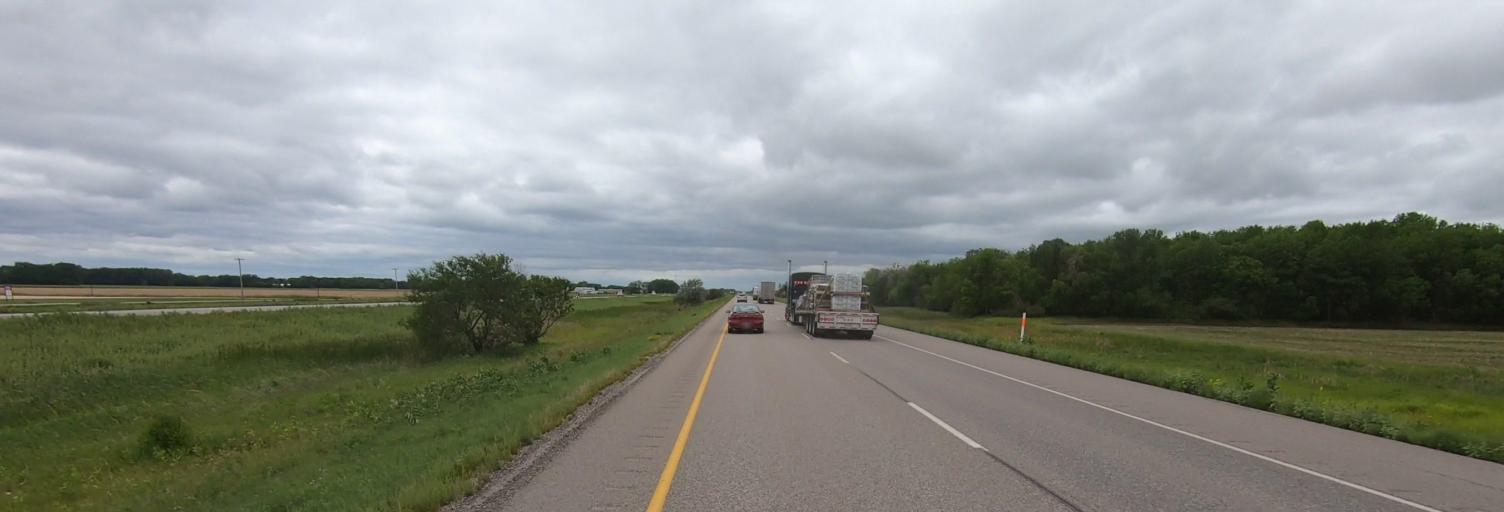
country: CA
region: Manitoba
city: Portage la Prairie
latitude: 49.9741
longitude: -98.1721
